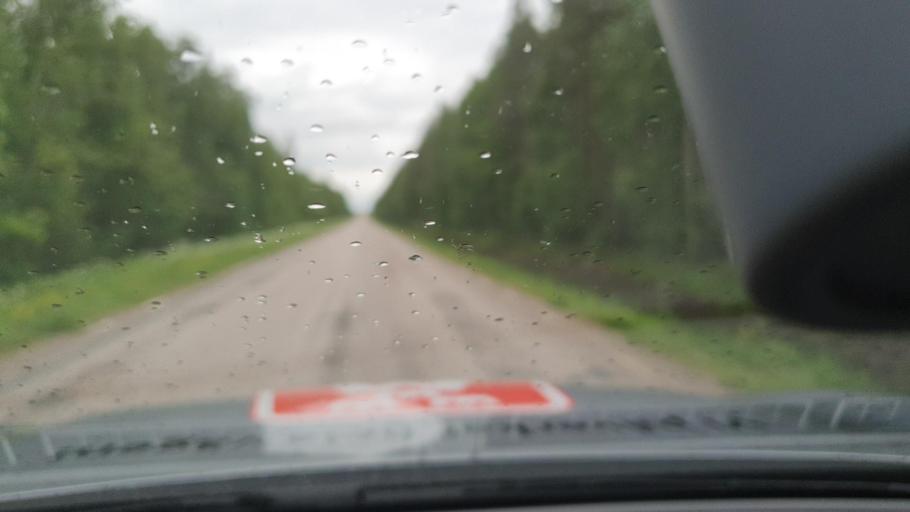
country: SE
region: Norrbotten
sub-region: Overkalix Kommun
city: OEverkalix
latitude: 66.3694
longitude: 22.8009
